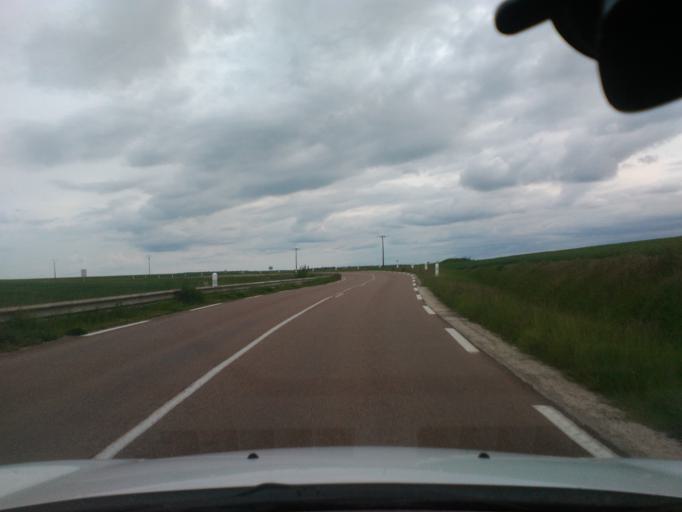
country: FR
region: Champagne-Ardenne
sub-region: Departement de l'Aube
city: Bar-sur-Aube
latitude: 48.2217
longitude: 4.8142
